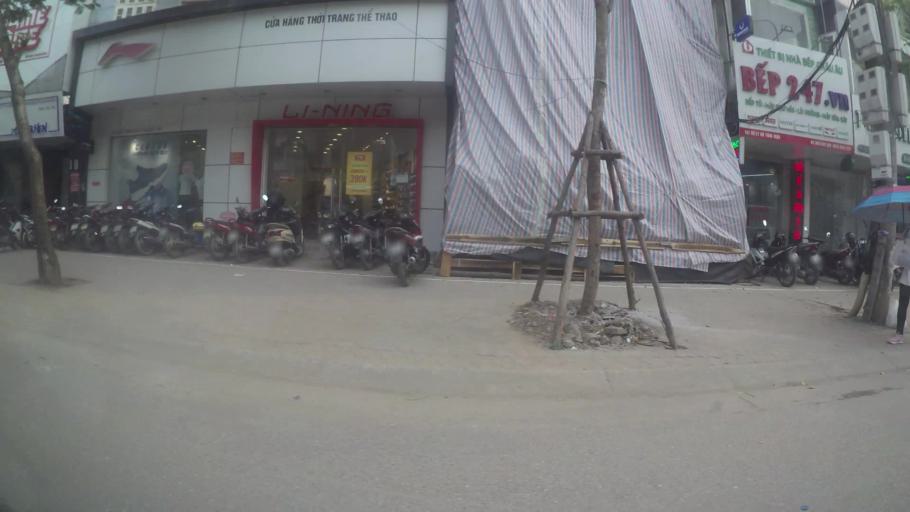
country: VN
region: Ha Noi
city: Cau Dien
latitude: 21.0366
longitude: 105.7776
